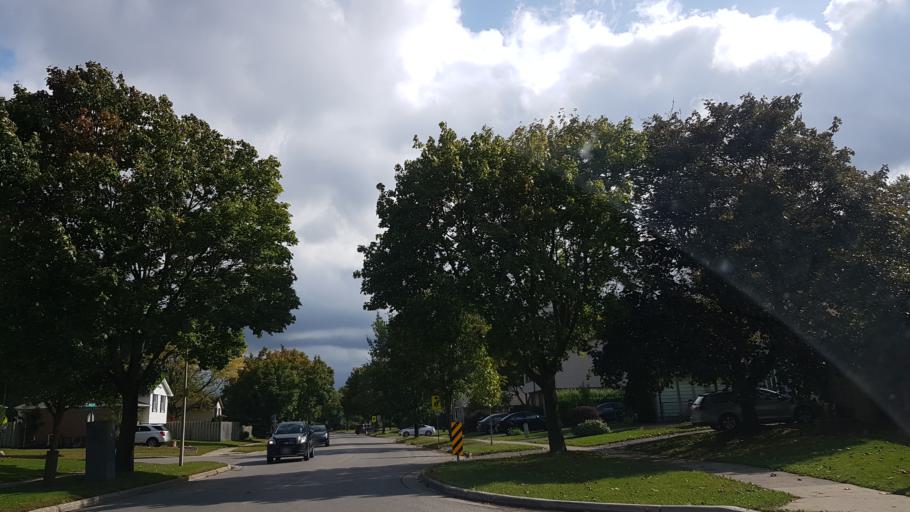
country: CA
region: Ontario
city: London
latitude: 42.9369
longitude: -81.2384
